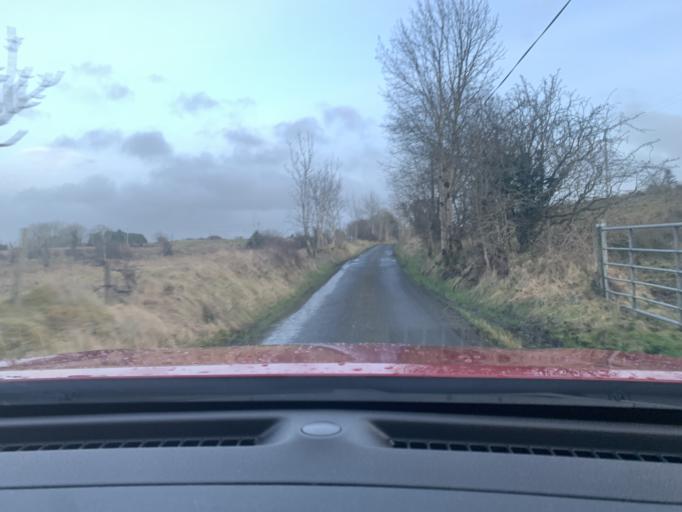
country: IE
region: Connaught
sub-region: Sligo
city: Ballymote
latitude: 53.9926
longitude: -8.4581
